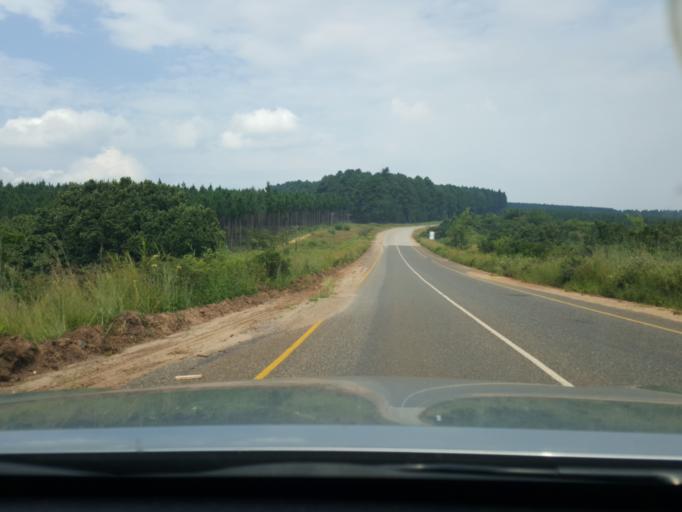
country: ZA
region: Mpumalanga
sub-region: Ehlanzeni District
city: White River
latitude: -25.2446
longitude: 30.9548
